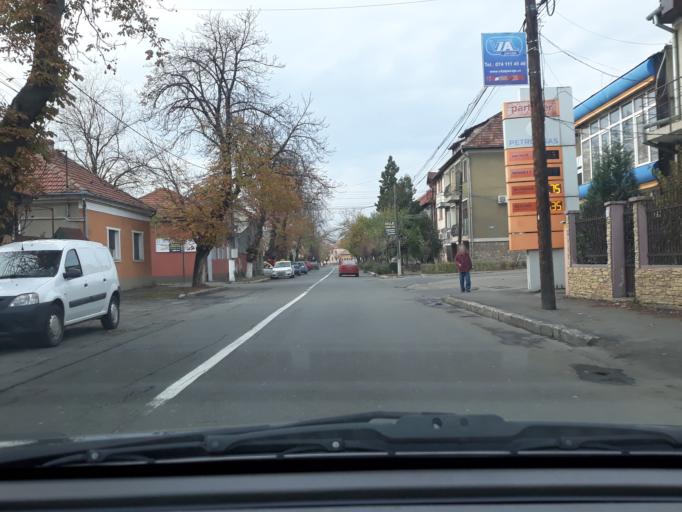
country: RO
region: Bihor
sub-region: Comuna Biharea
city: Oradea
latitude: 47.0454
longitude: 21.9478
